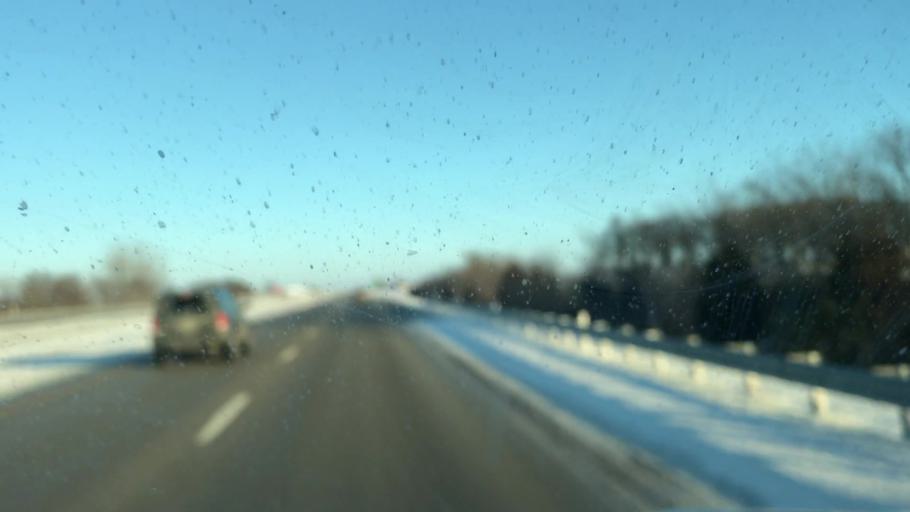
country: US
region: Missouri
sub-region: Buchanan County
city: Saint Joseph
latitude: 39.7476
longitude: -94.7015
